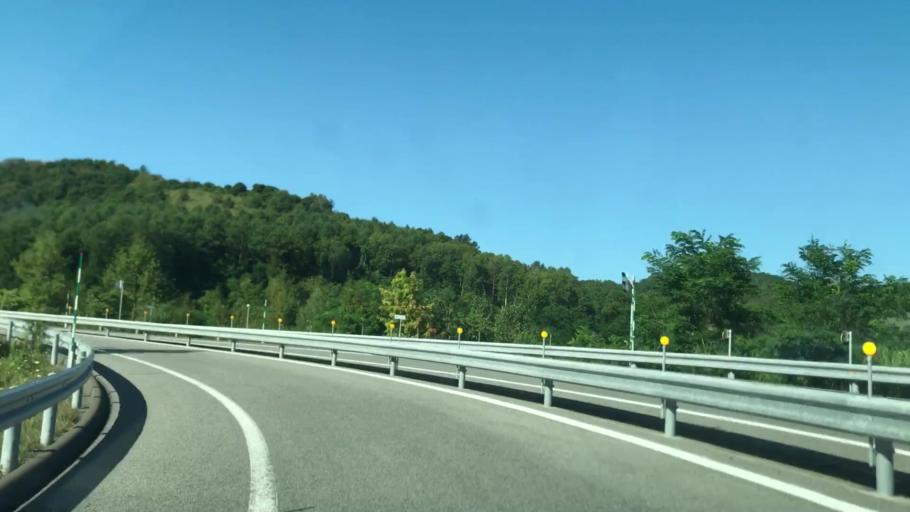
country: JP
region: Hokkaido
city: Date
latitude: 42.5572
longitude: 140.7726
